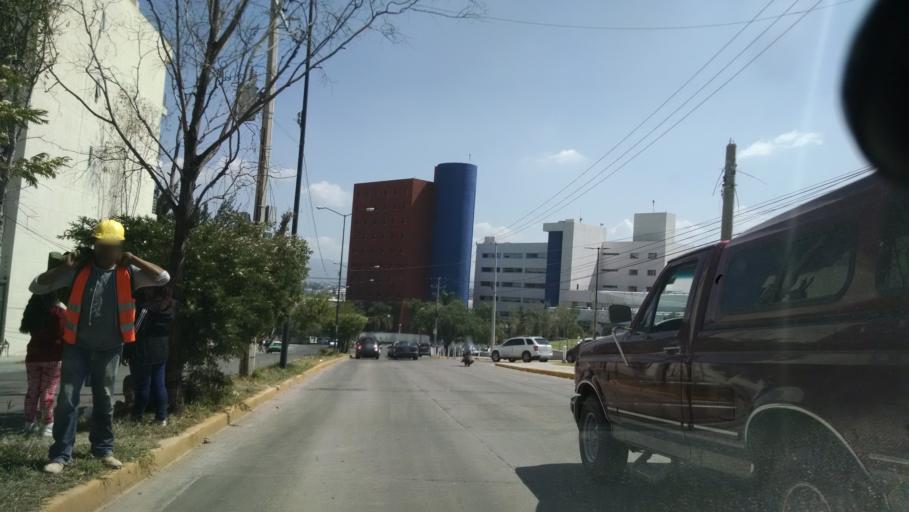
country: MX
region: Guanajuato
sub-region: Leon
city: La Ermita
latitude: 21.1581
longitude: -101.7027
